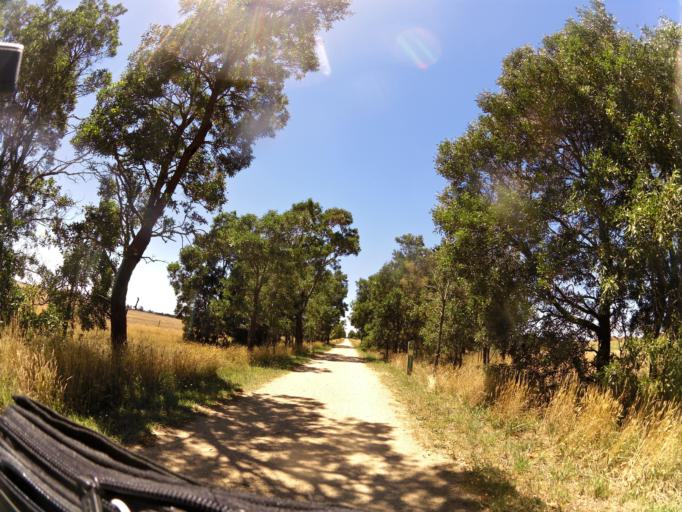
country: AU
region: Victoria
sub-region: Ballarat North
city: Newington
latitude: -37.5454
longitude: 143.7640
